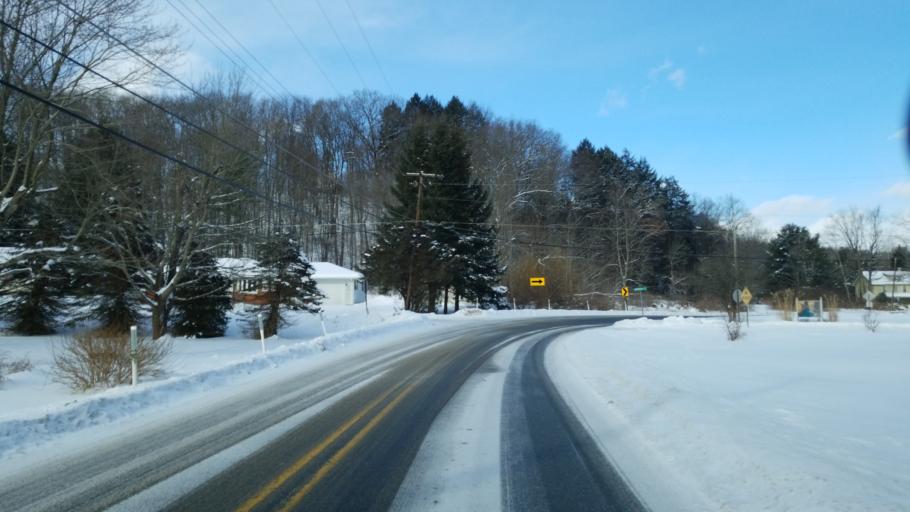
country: US
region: Pennsylvania
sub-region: Clearfield County
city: Hyde
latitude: 41.0039
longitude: -78.4665
